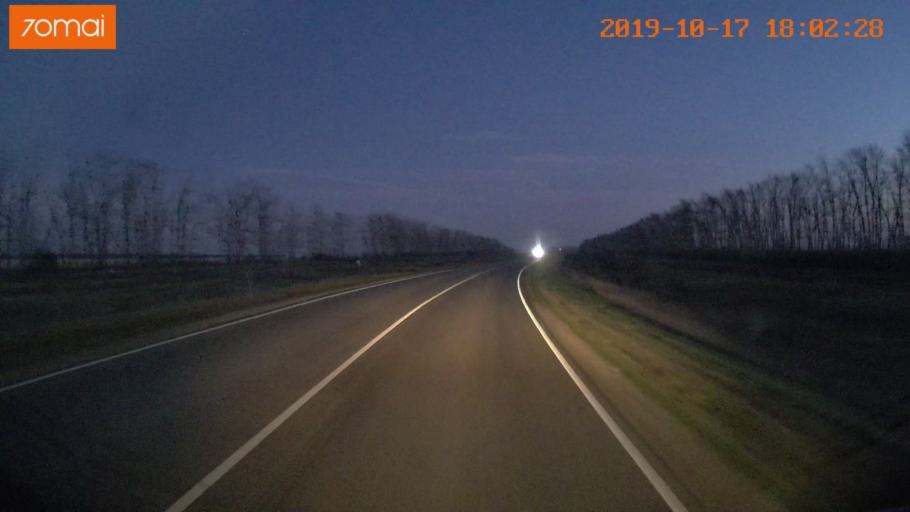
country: RU
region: Tula
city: Kurkino
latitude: 53.5065
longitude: 38.6144
